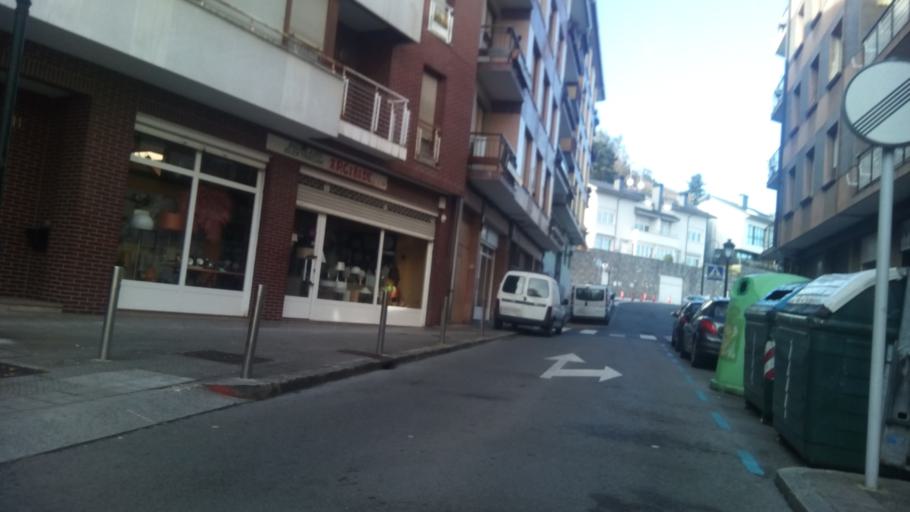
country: ES
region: Basque Country
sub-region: Bizkaia
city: Gernika-Lumo
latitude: 43.3168
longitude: -2.6800
